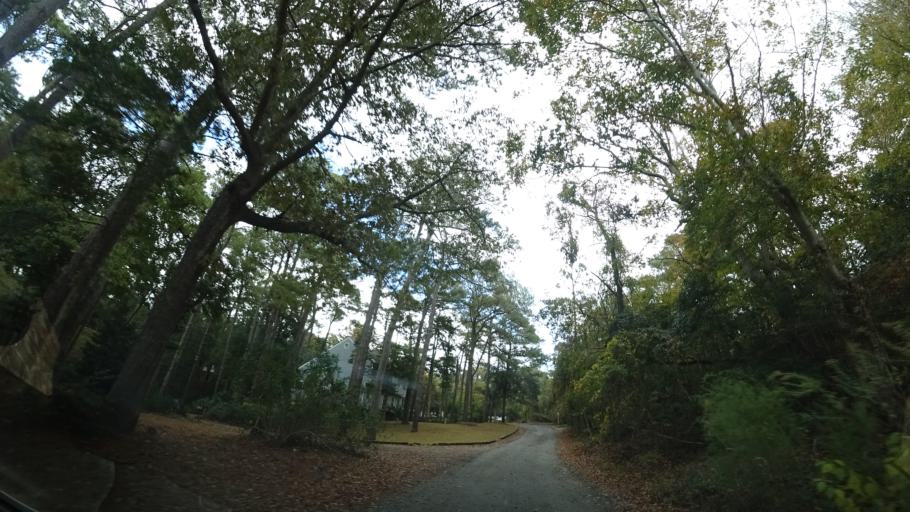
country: US
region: North Carolina
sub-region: Dare County
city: Kill Devil Hills
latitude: 35.9902
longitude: -75.6629
